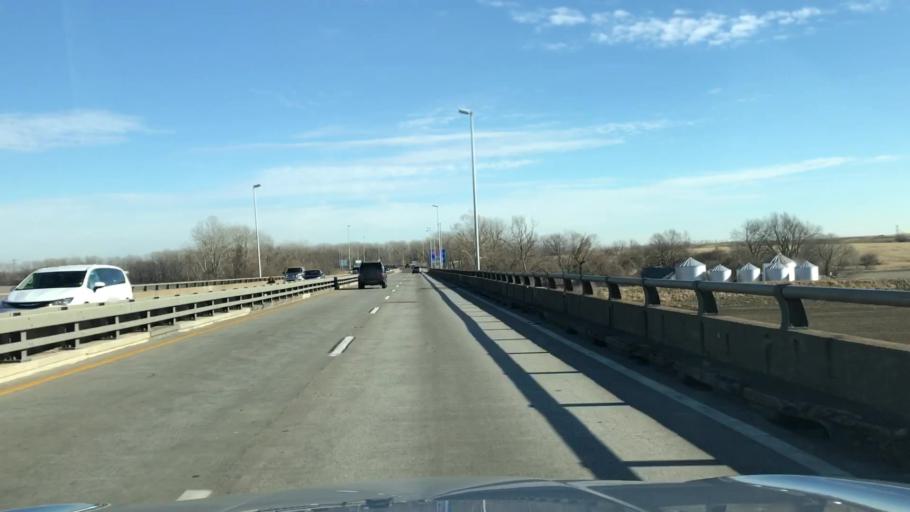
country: US
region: Missouri
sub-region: Saint Louis County
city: Glasgow Village
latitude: 38.7619
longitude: -90.1648
